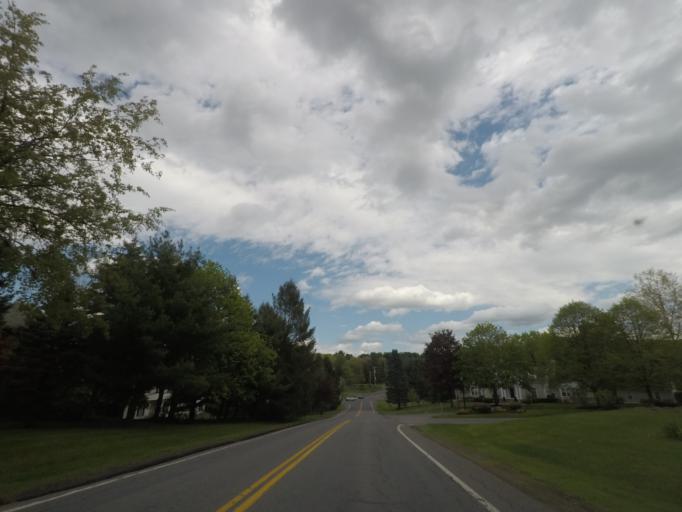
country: US
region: New York
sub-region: Albany County
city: Voorheesville
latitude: 42.6709
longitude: -73.9150
